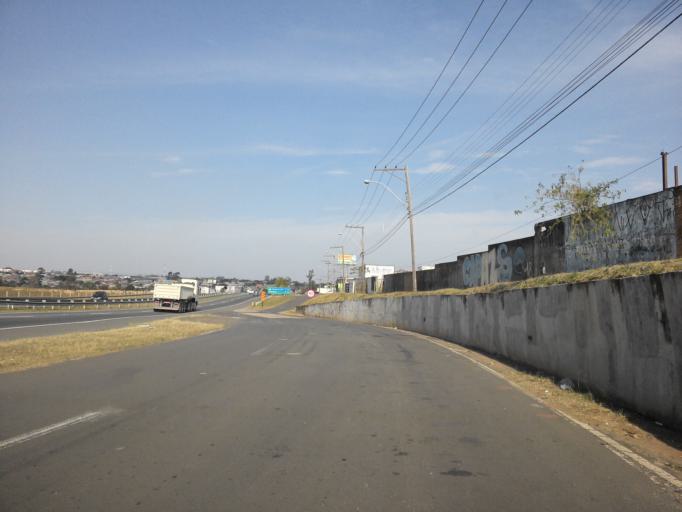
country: BR
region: Sao Paulo
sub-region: Hortolandia
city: Hortolandia
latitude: -22.9032
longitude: -47.2257
